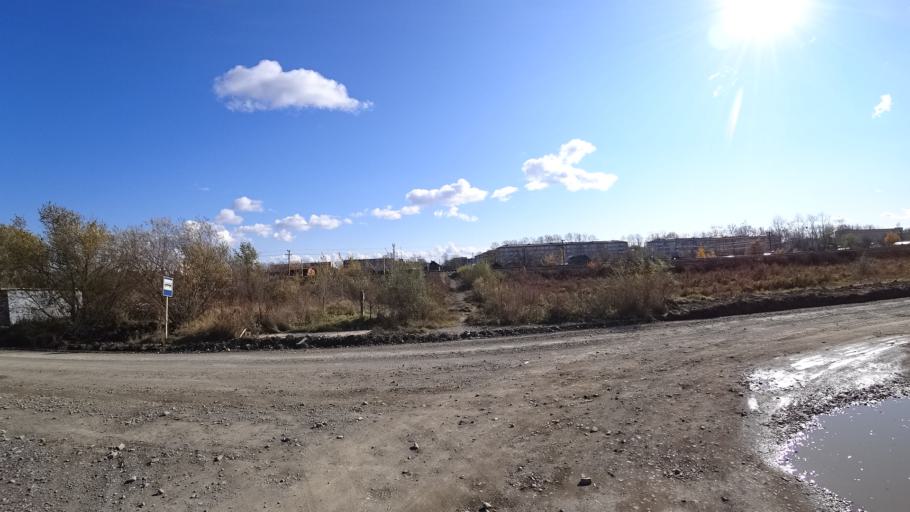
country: RU
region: Khabarovsk Krai
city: Amursk
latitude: 50.1018
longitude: 136.5073
